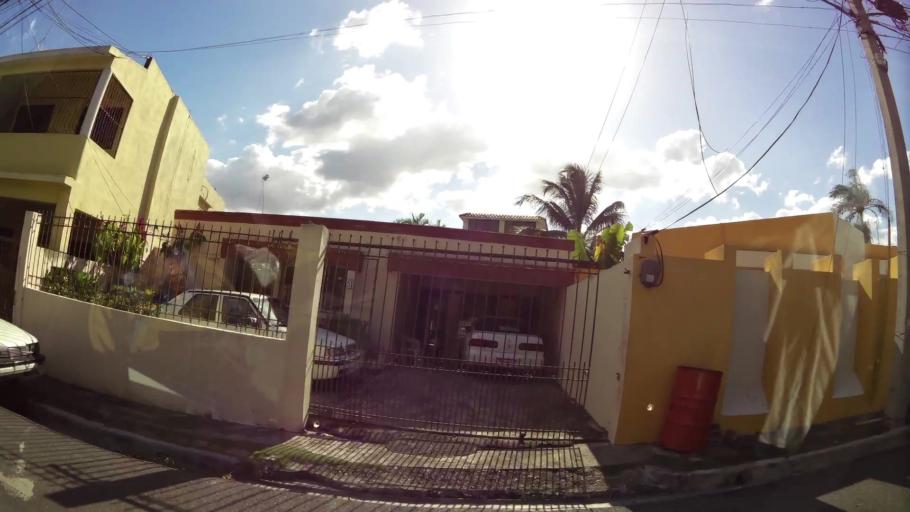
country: DO
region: Nacional
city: Santo Domingo
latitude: 18.5089
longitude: -69.9866
